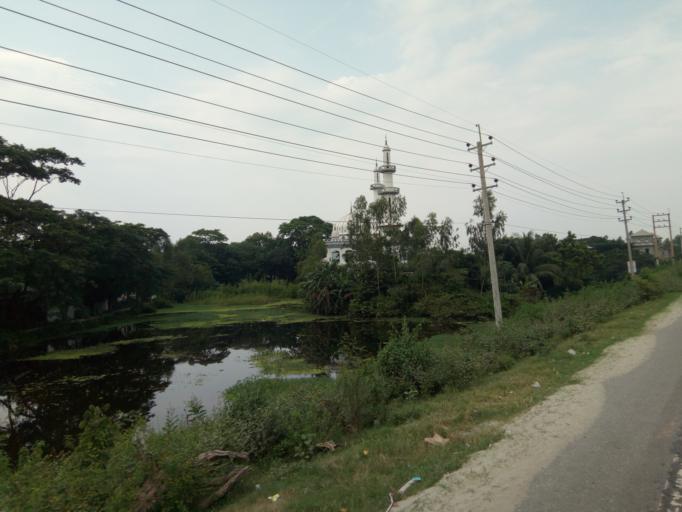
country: BD
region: Dhaka
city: Dohar
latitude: 23.5447
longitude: 90.2972
